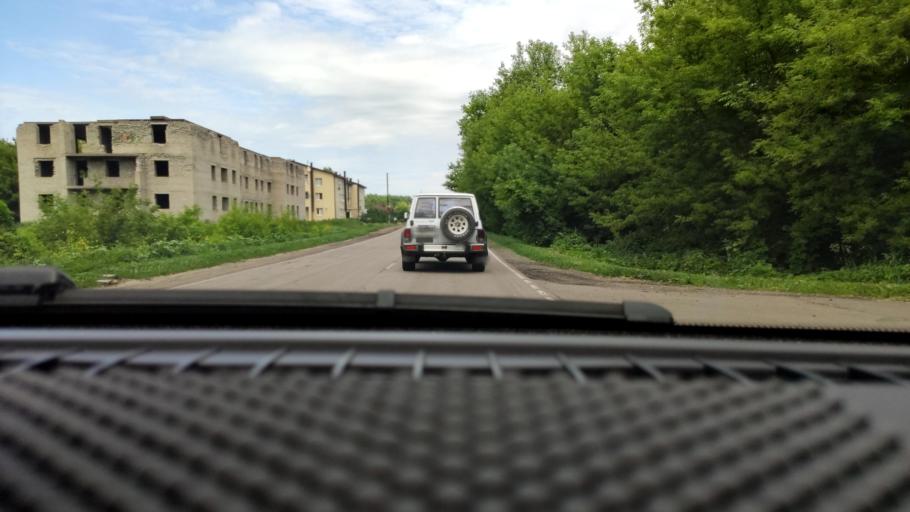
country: RU
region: Voronezj
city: Panino
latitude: 51.6570
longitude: 40.1233
